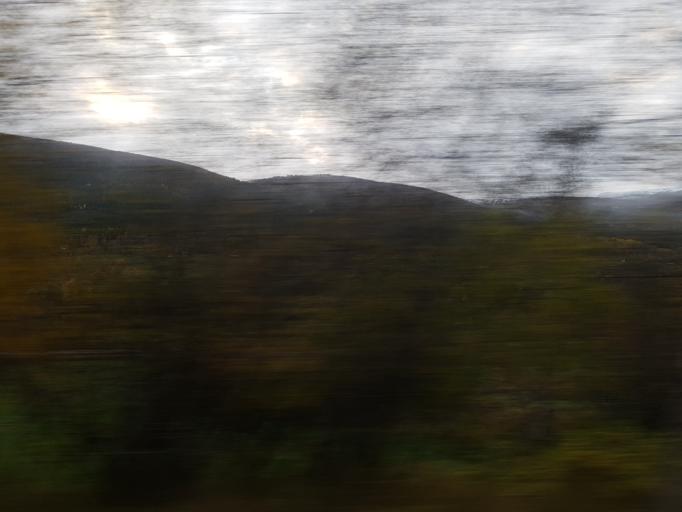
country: NO
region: Oppland
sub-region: Dovre
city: Dovre
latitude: 61.9941
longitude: 9.2329
